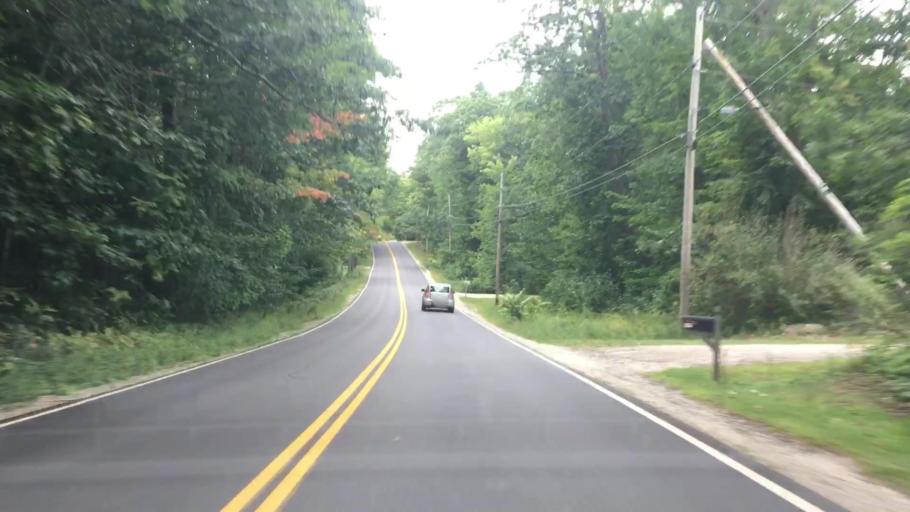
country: US
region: Maine
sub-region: Cumberland County
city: Cumberland Center
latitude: 43.8762
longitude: -70.2451
